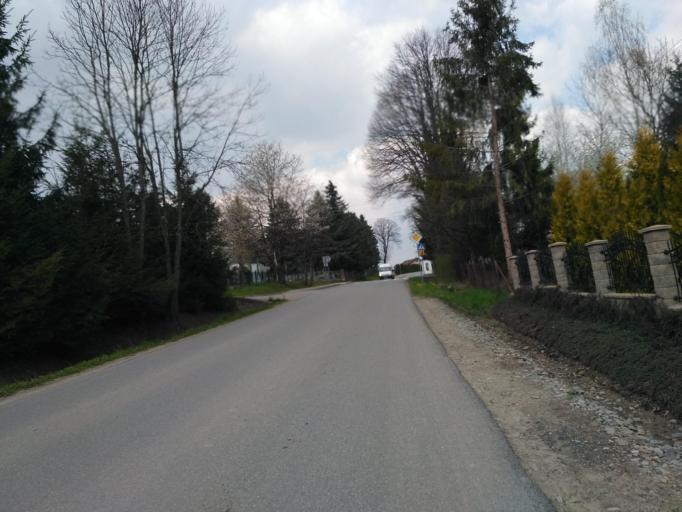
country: PL
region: Subcarpathian Voivodeship
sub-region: Powiat sanocki
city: Strachocina
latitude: 49.6025
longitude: 22.0928
